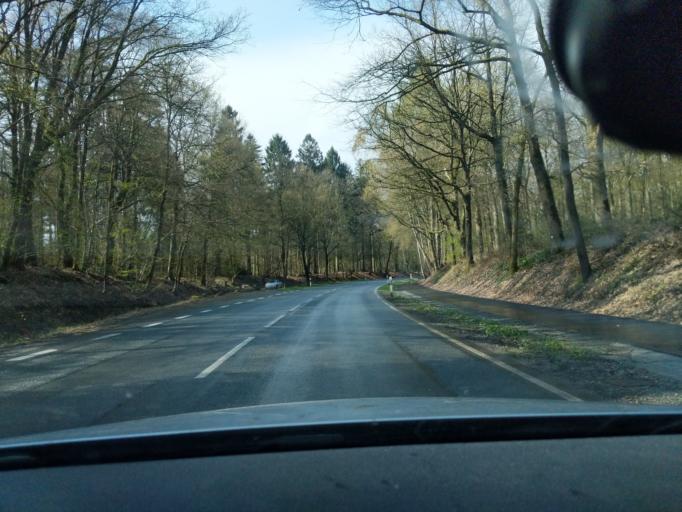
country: DE
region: Lower Saxony
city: Harsefeld
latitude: 53.4642
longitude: 9.4999
